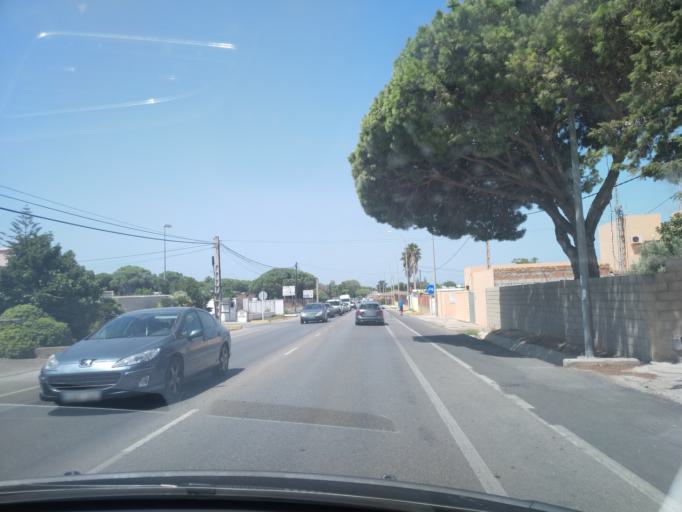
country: ES
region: Andalusia
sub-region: Provincia de Cadiz
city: Chiclana de la Frontera
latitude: 36.3941
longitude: -6.1496
